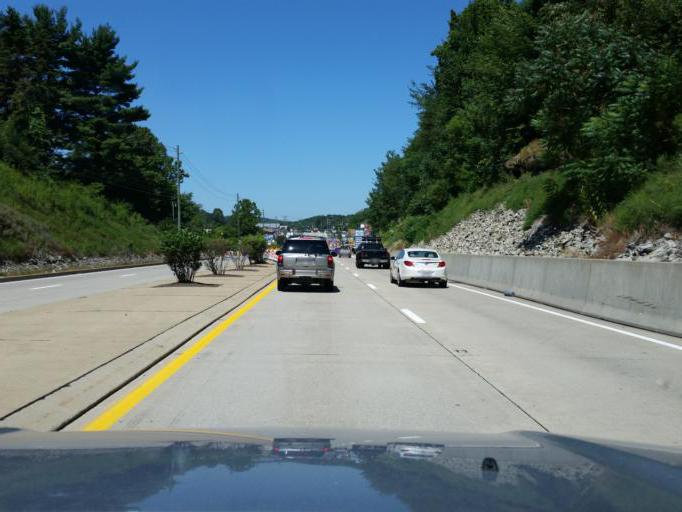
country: US
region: Pennsylvania
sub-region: Westmoreland County
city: Murrysville
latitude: 40.4208
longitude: -79.6567
